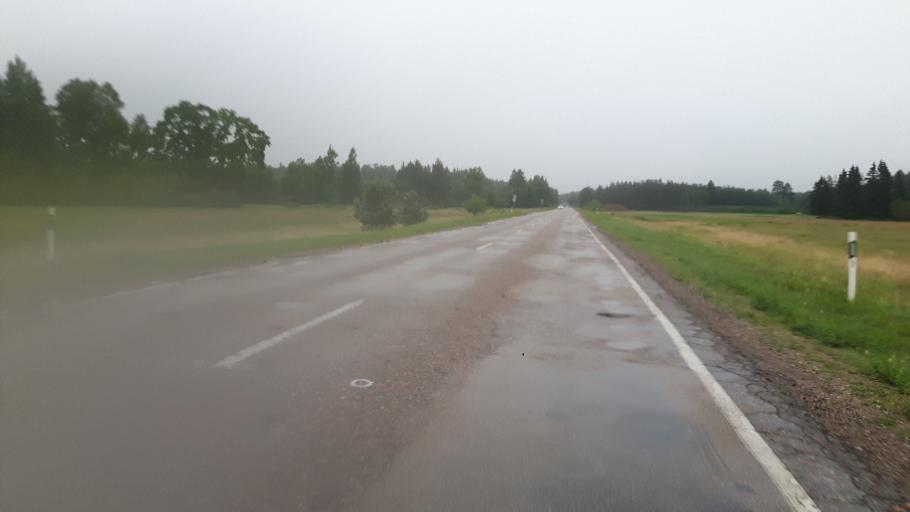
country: LV
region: Rucavas
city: Rucava
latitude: 56.1010
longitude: 21.1337
